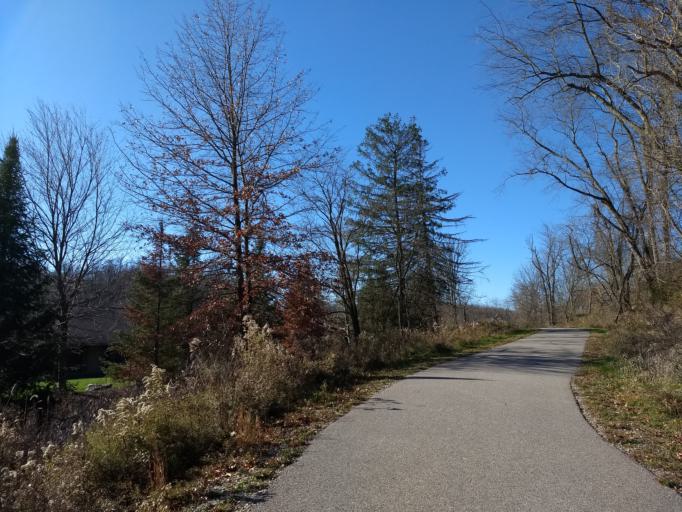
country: US
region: Pennsylvania
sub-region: Allegheny County
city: South Park Township
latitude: 40.2893
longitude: -80.0240
